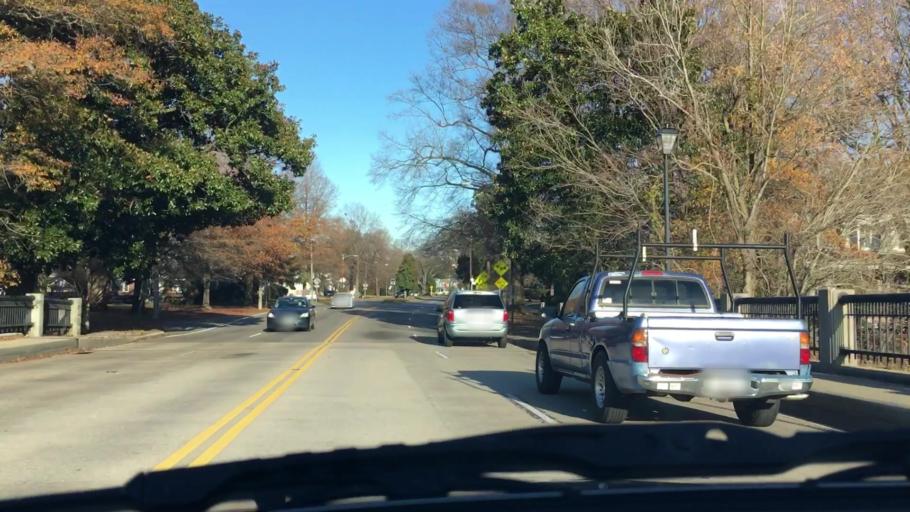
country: US
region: Virginia
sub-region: City of Norfolk
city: Norfolk
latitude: 36.8738
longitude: -76.2720
